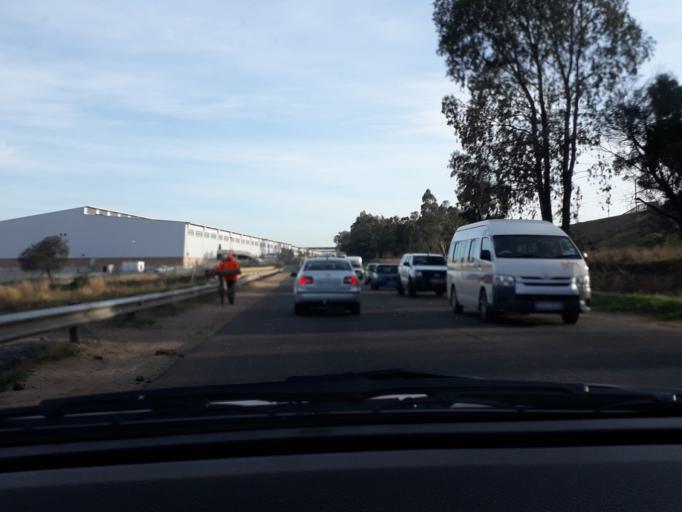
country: ZA
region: Gauteng
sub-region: City of Johannesburg Metropolitan Municipality
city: Midrand
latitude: -25.9310
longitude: 28.1484
